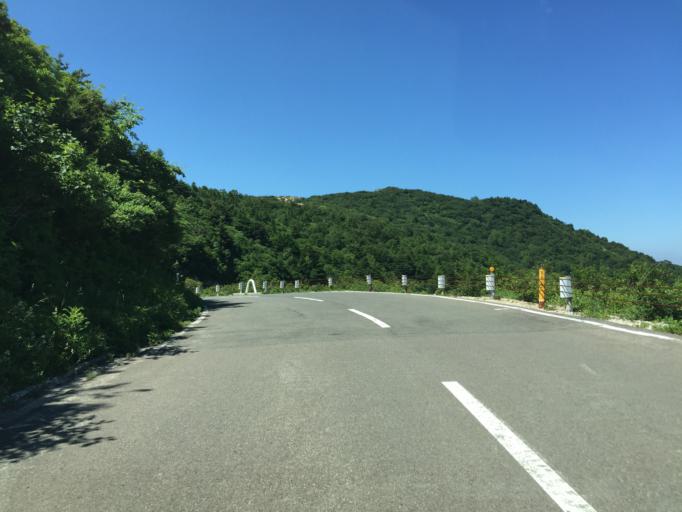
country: JP
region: Fukushima
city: Fukushima-shi
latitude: 37.7369
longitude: 140.2686
